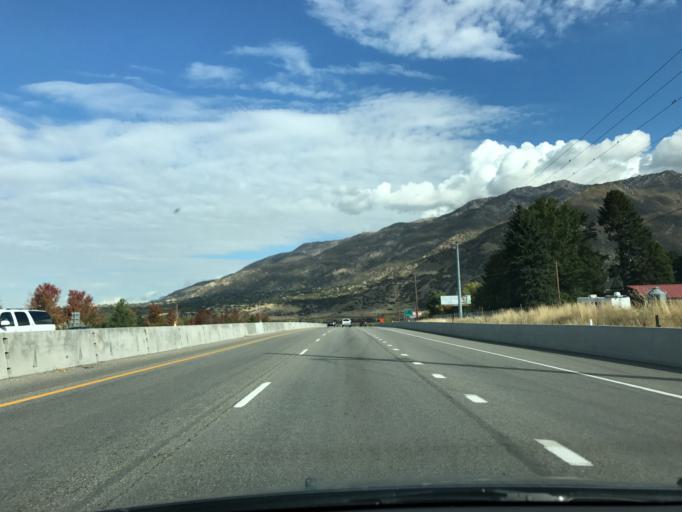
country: US
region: Utah
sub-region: Davis County
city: South Weber
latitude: 41.1183
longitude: -111.9085
